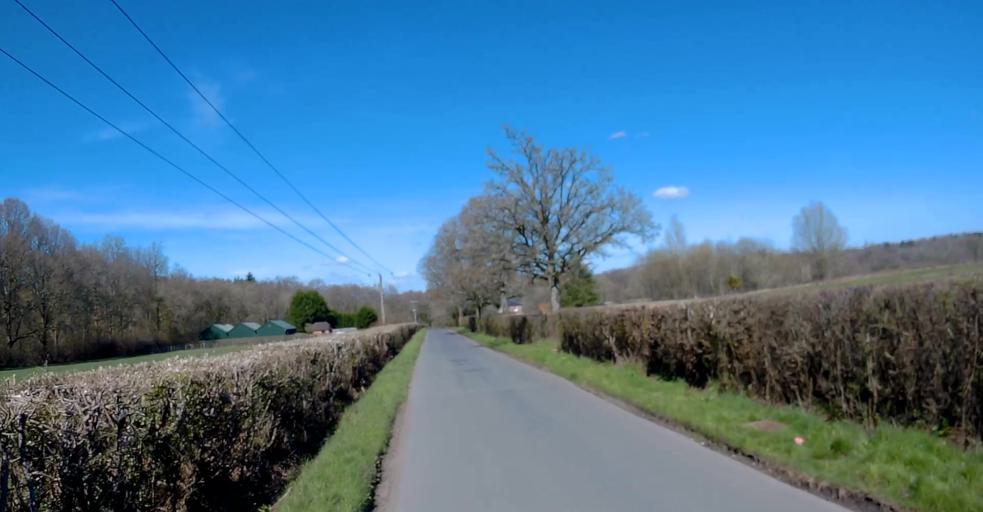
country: GB
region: England
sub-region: Surrey
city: Farnham
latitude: 51.1704
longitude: -0.8276
